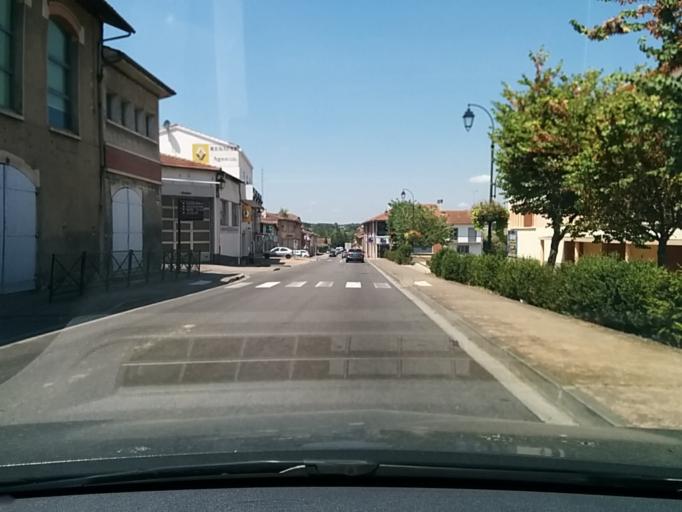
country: FR
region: Midi-Pyrenees
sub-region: Departement du Gers
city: Gimont
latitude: 43.6270
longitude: 0.8777
